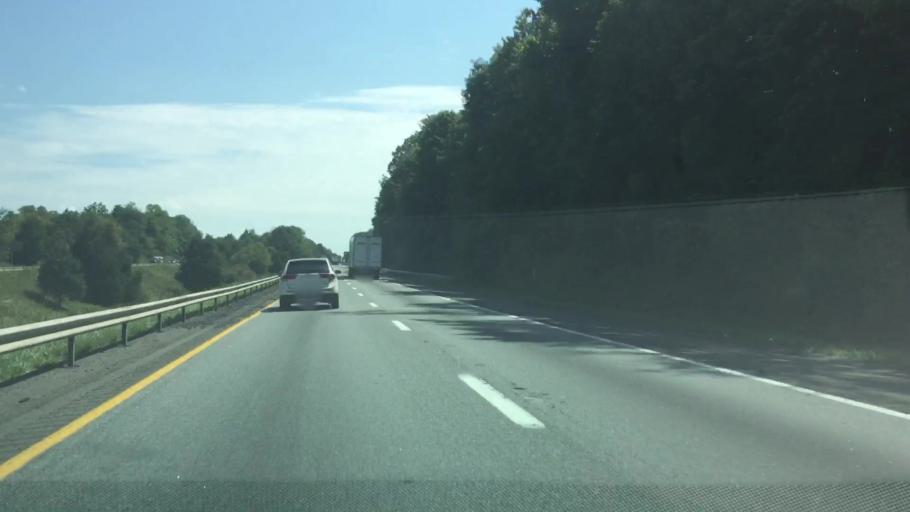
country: US
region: Virginia
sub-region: City of Radford
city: Radford
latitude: 37.0993
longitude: -80.5507
